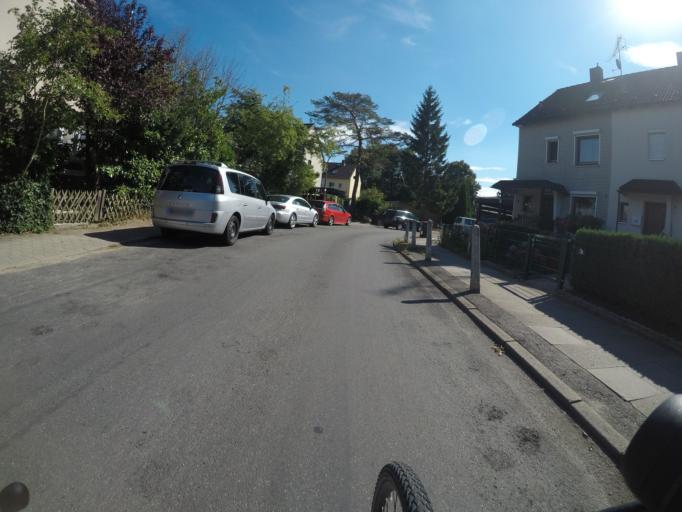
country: DE
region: Hamburg
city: Farmsen-Berne
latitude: 53.6059
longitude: 10.1374
